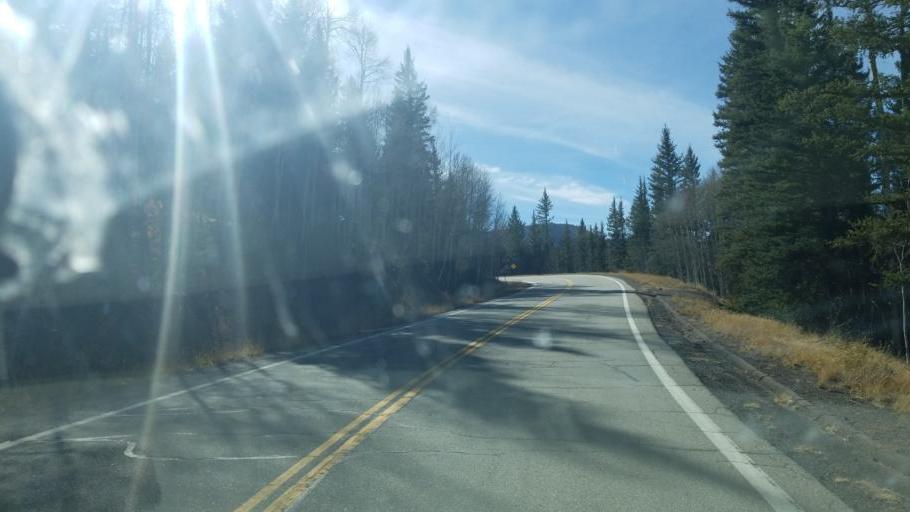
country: US
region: New Mexico
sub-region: Rio Arriba County
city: Chama
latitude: 37.1229
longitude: -106.3621
